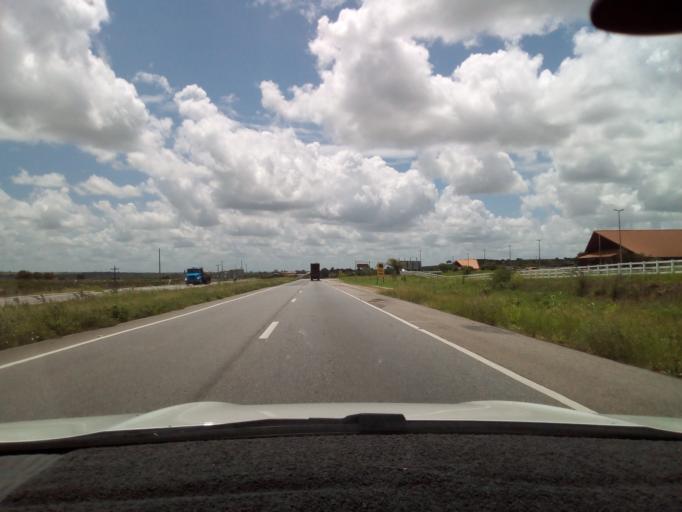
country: BR
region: Paraiba
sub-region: Gurinhem
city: Gurinhem
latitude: -7.1716
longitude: -35.3864
